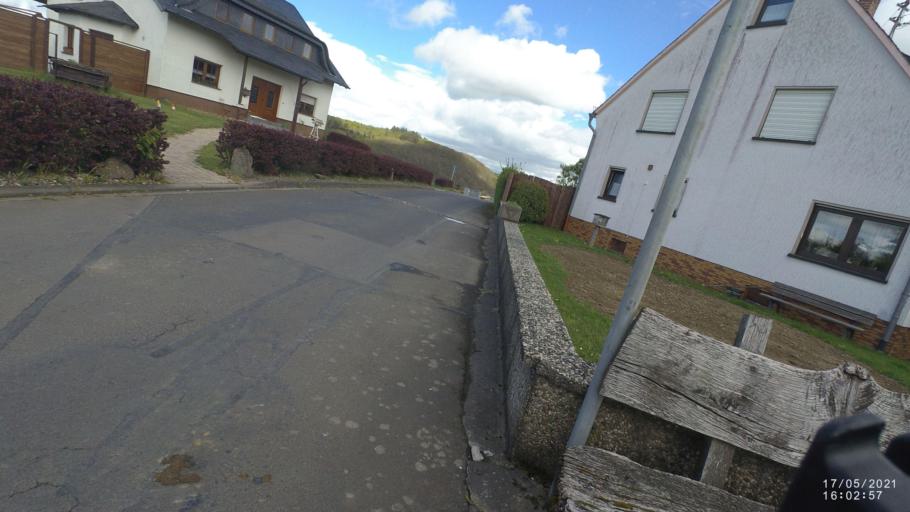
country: DE
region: Rheinland-Pfalz
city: Lind
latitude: 50.3089
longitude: 7.0441
